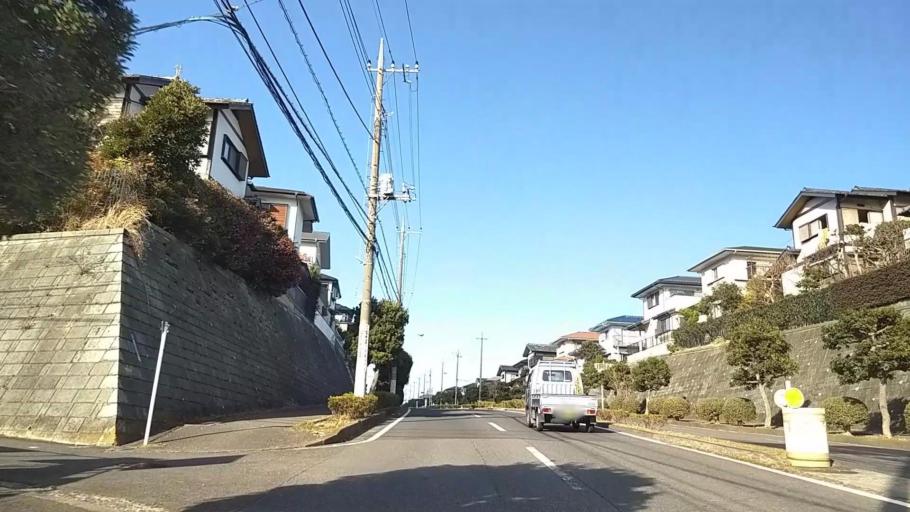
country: JP
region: Kanagawa
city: Atsugi
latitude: 35.4349
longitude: 139.3307
